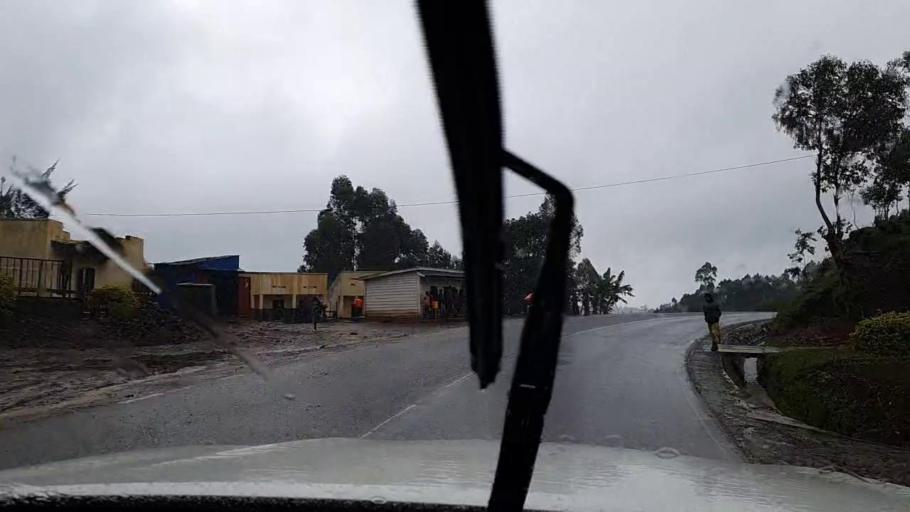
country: RW
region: Western Province
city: Cyangugu
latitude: -2.4630
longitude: 28.9998
